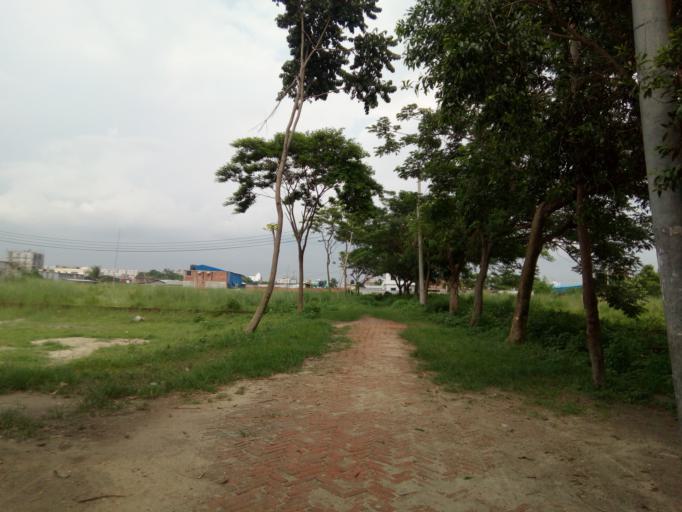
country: BD
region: Dhaka
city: Azimpur
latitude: 23.7553
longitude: 90.3429
